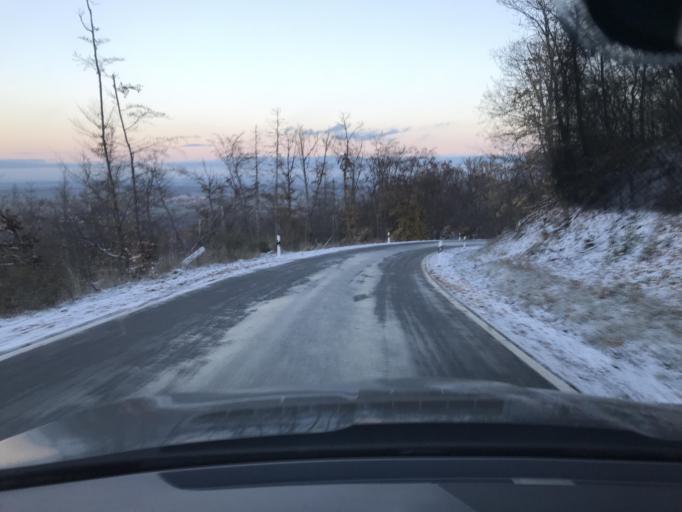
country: DE
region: Saxony-Anhalt
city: Timmenrode
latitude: 51.7456
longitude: 11.0094
